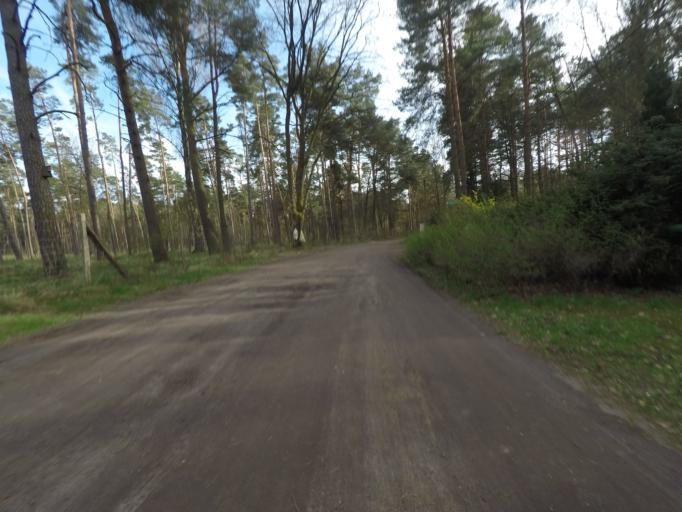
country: DE
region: Brandenburg
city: Marienwerder
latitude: 52.8504
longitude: 13.6530
